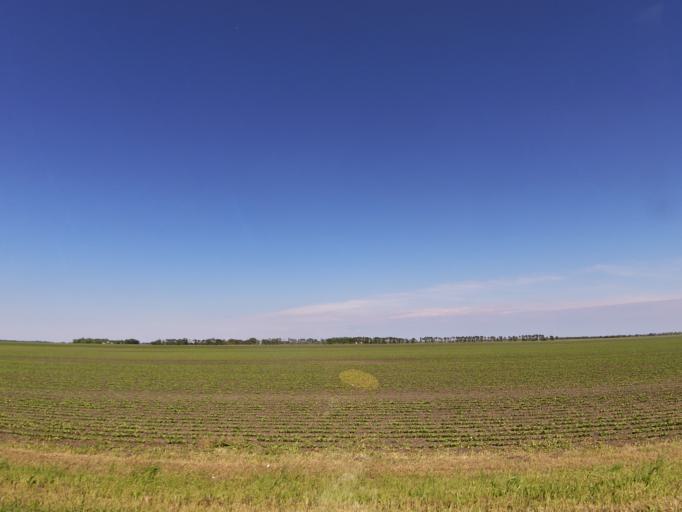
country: US
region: North Dakota
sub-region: Walsh County
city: Grafton
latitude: 48.3423
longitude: -97.2558
